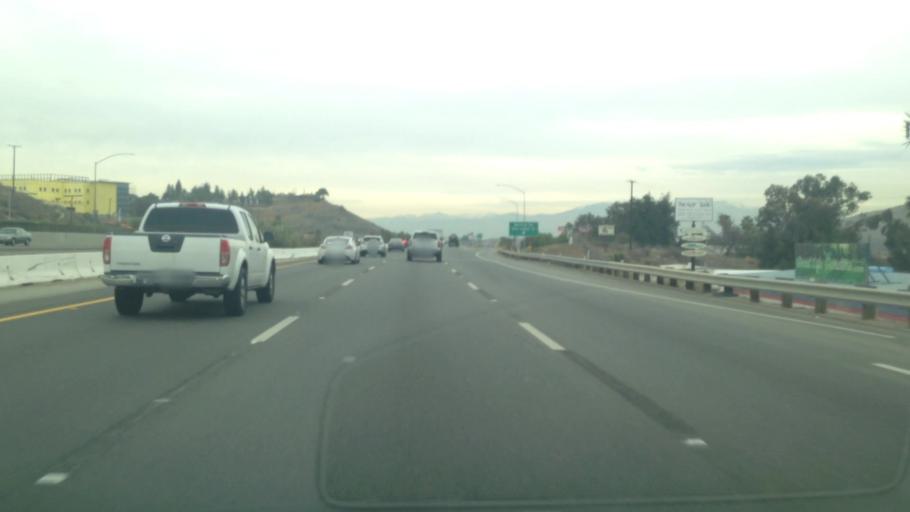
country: US
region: California
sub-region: Riverside County
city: El Cerrito
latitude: 33.8024
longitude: -117.5048
